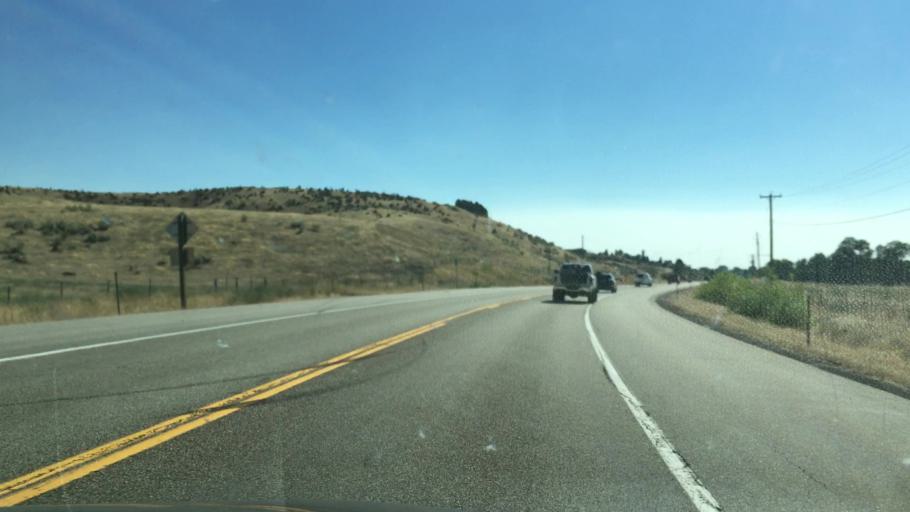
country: US
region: Idaho
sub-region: Ada County
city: Eagle
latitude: 43.7285
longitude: -116.3055
